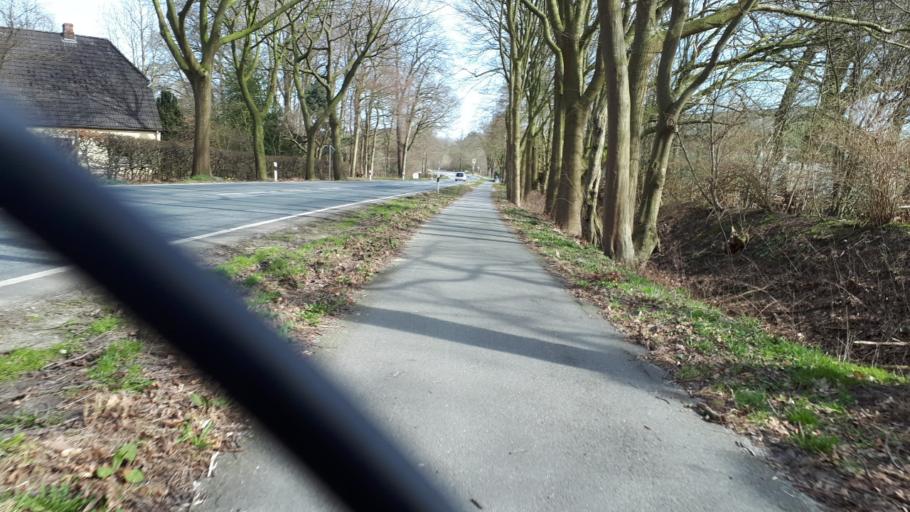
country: DE
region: Lower Saxony
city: Ganderkesee
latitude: 53.0466
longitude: 8.5015
